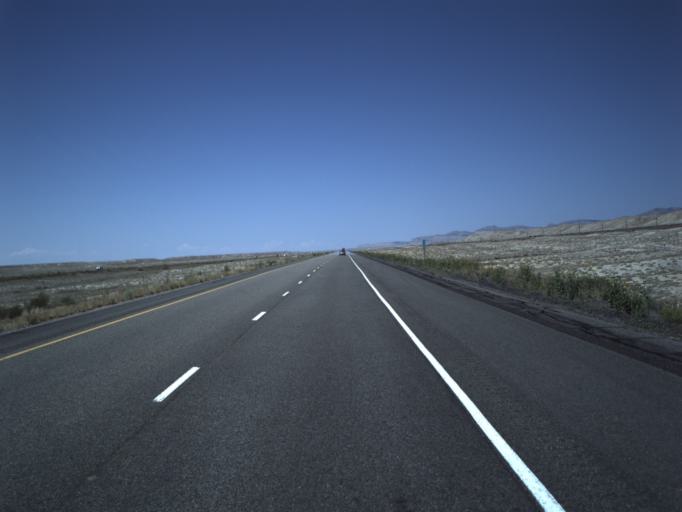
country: US
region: Utah
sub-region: Grand County
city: Moab
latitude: 38.9333
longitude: -109.4369
